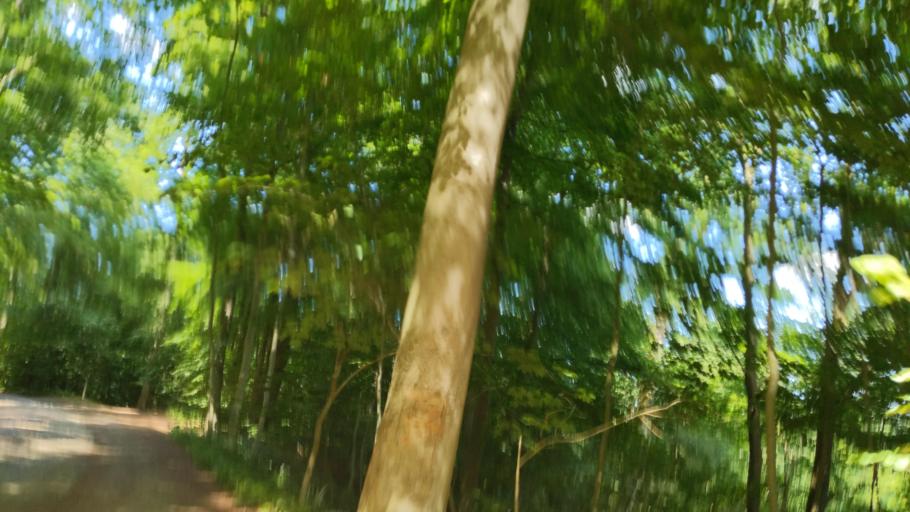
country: DE
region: Schleswig-Holstein
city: Schmilau
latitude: 53.6831
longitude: 10.7529
